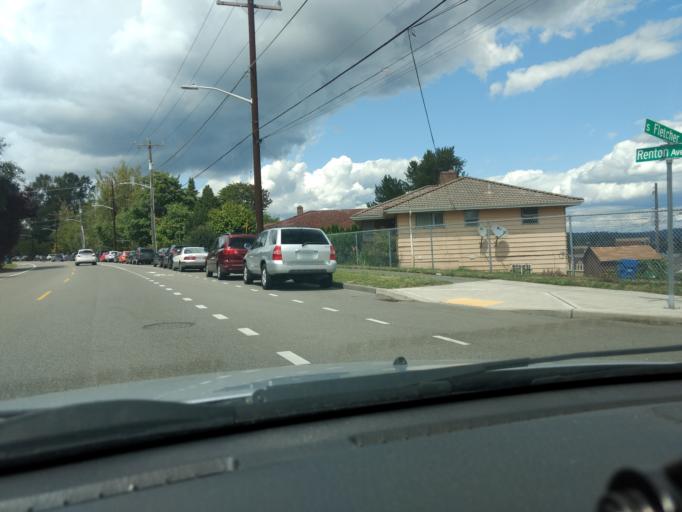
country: US
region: Washington
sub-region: King County
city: Bryn Mawr-Skyway
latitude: 47.5191
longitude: -122.2715
